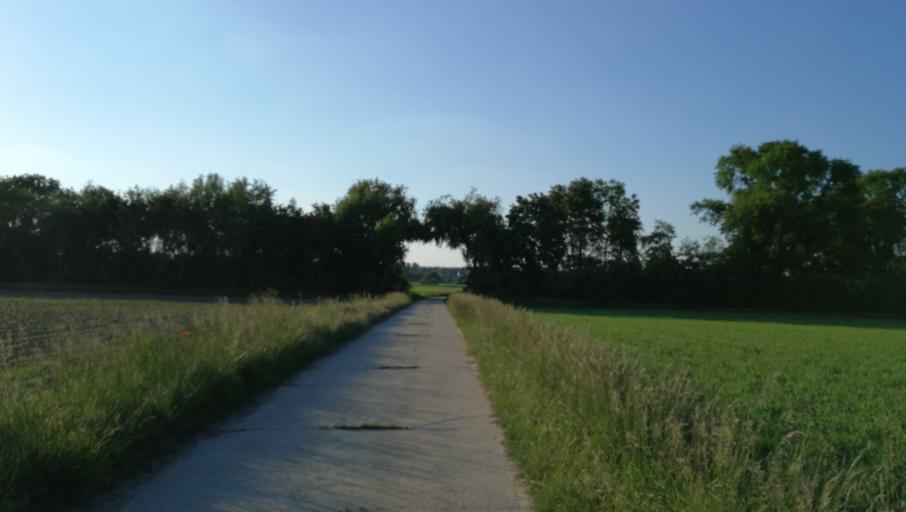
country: DE
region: Baden-Wuerttemberg
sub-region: Karlsruhe Region
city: Altlussheim
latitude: 49.3221
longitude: 8.4735
